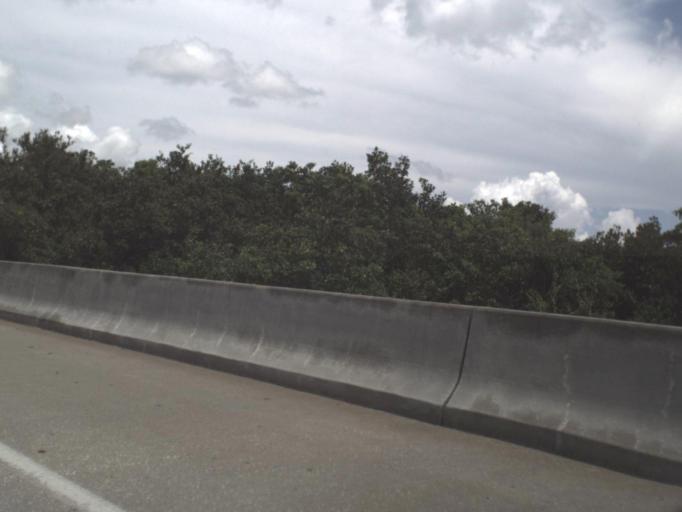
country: US
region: Florida
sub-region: Pinellas County
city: South Highpoint
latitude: 27.9227
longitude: -82.6982
